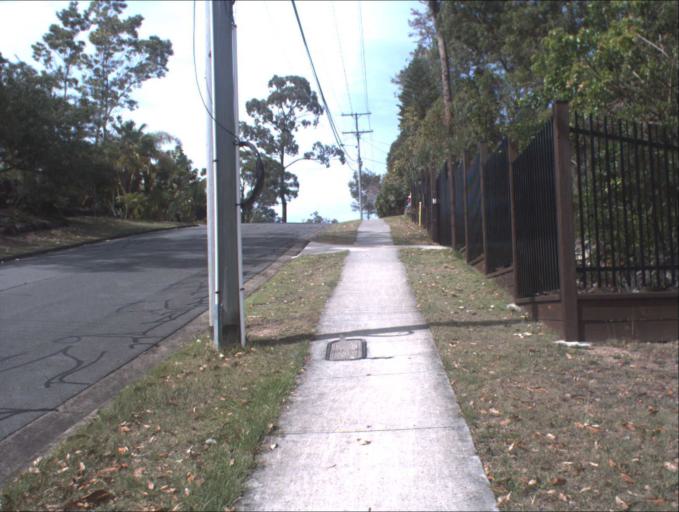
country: AU
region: Queensland
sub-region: Logan
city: Slacks Creek
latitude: -27.6262
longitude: 153.1502
